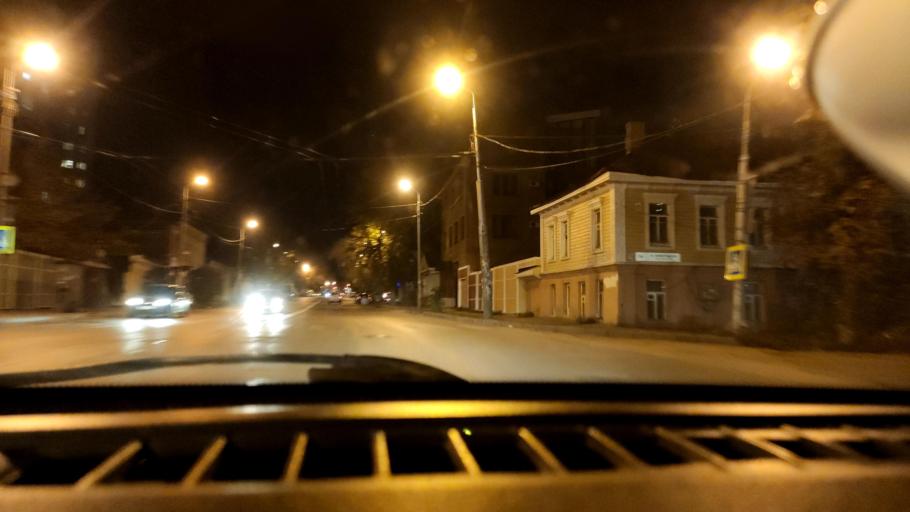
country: RU
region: Samara
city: Samara
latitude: 53.1836
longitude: 50.1067
